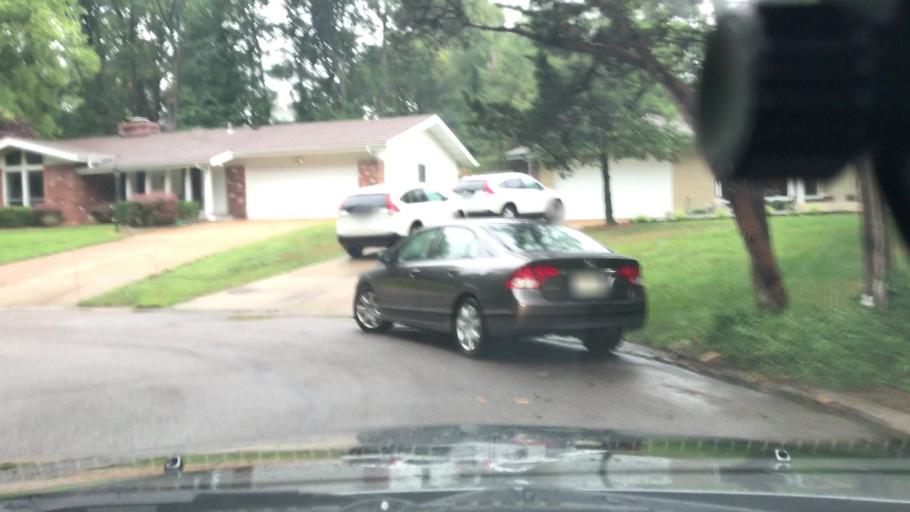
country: US
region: Missouri
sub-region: Saint Louis County
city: Maryland Heights
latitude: 38.6927
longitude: -90.4566
